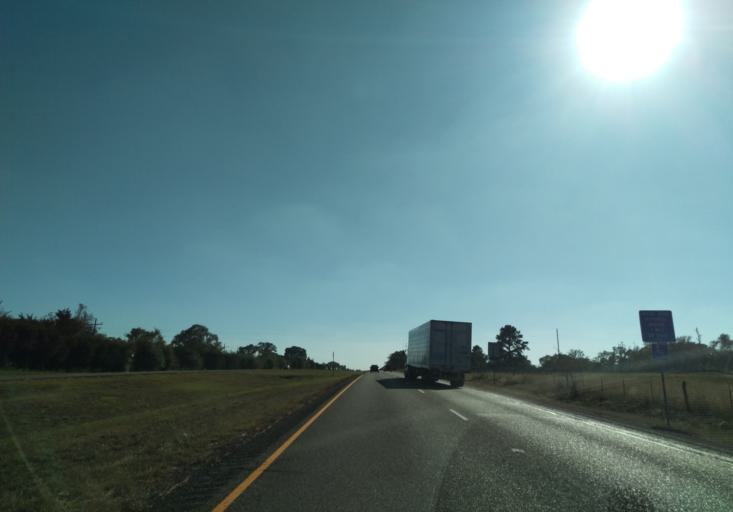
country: US
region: Texas
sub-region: Grimes County
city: Navasota
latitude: 30.2464
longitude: -96.0475
